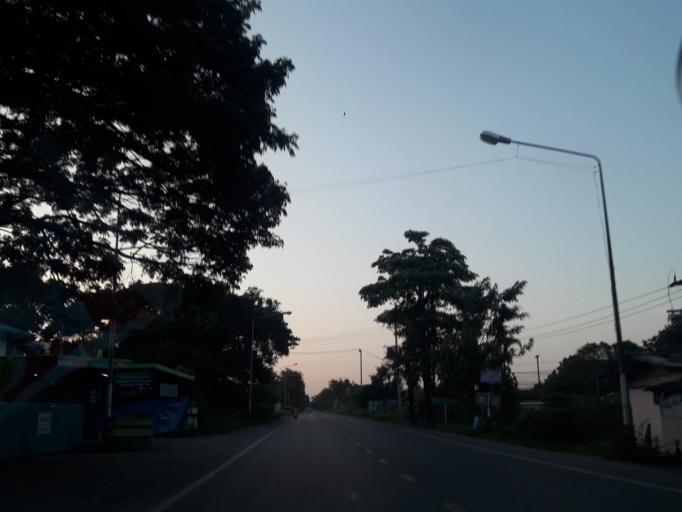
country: TH
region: Phra Nakhon Si Ayutthaya
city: Maha Rat
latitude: 14.5355
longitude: 100.5301
